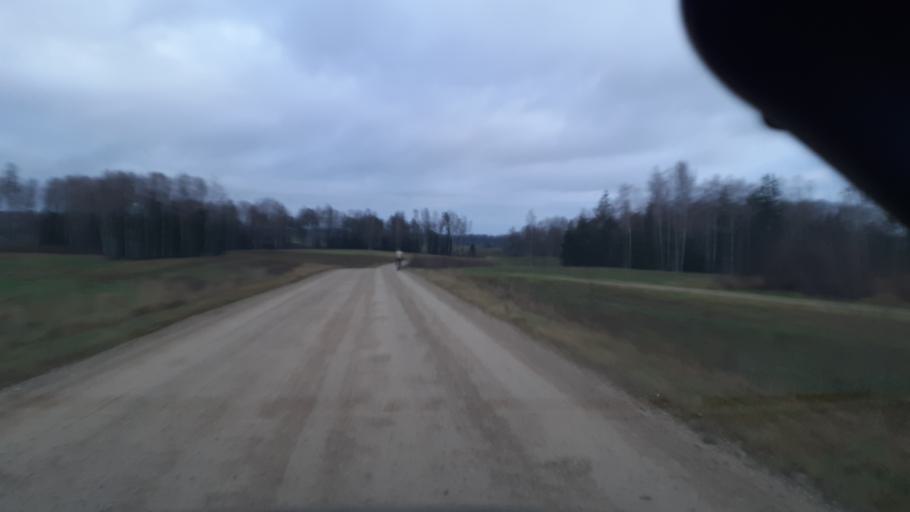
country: LV
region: Alsunga
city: Alsunga
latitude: 56.8927
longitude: 21.7024
